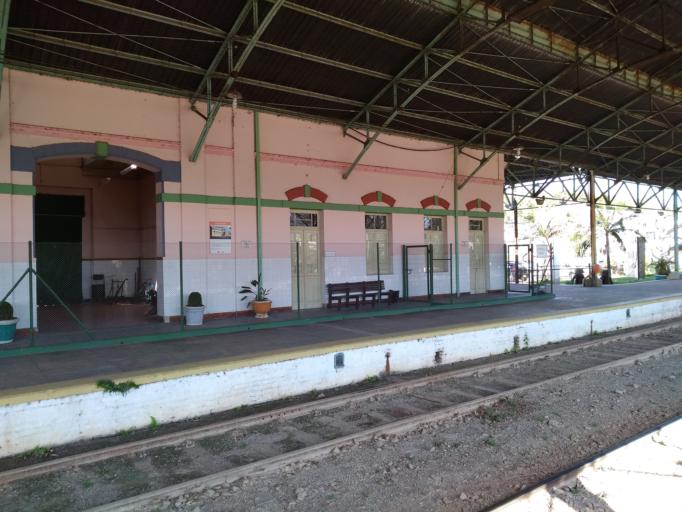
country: BR
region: Sao Paulo
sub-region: Valinhos
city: Valinhos
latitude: -22.9692
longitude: -46.9935
